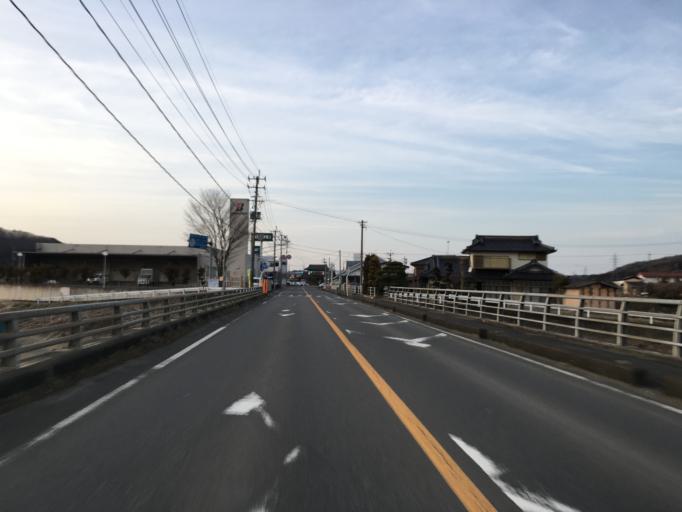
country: JP
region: Fukushima
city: Ishikawa
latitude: 37.0079
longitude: 140.3928
